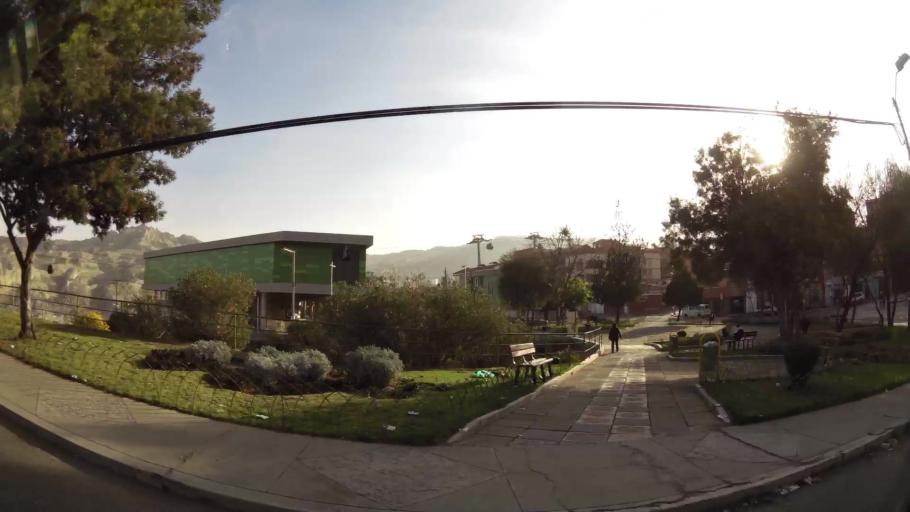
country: BO
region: La Paz
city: La Paz
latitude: -16.5208
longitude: -68.1095
